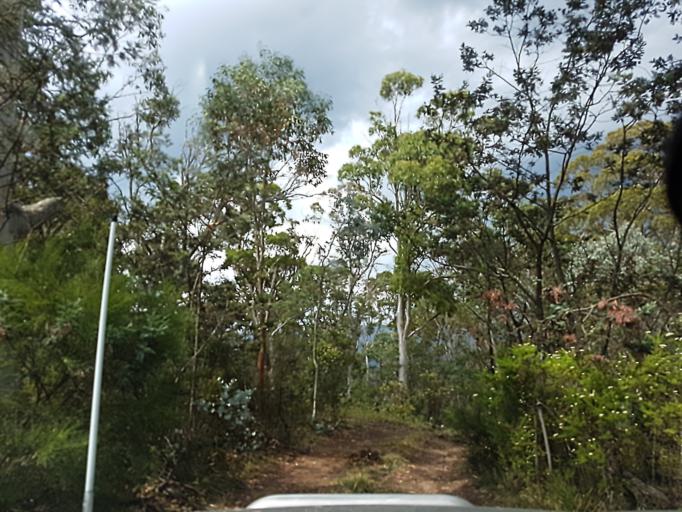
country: AU
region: New South Wales
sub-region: Snowy River
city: Jindabyne
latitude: -36.8795
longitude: 148.1865
